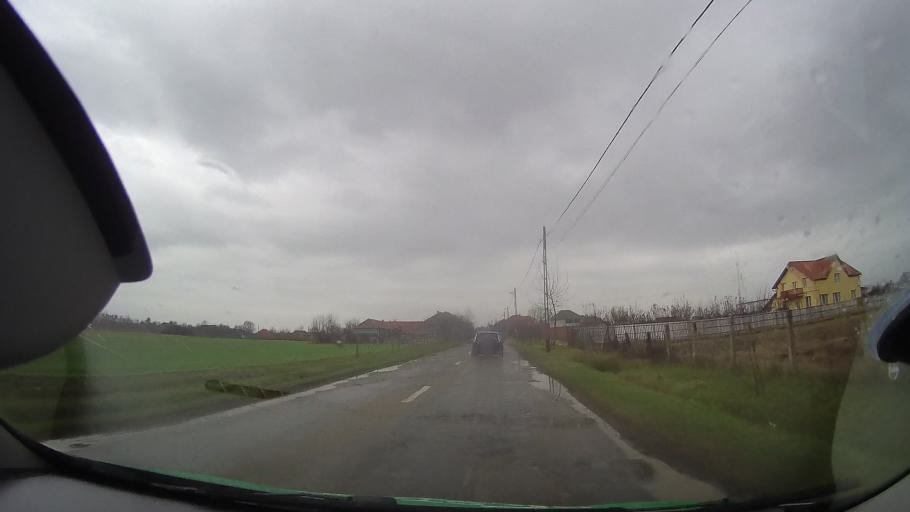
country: RO
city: Capalna
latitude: 46.7065
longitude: 22.0847
